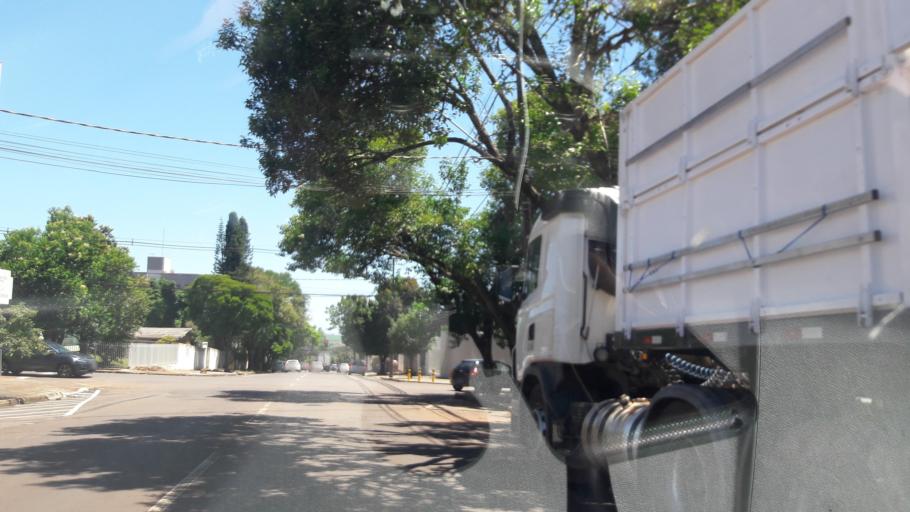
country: BR
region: Parana
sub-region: Cascavel
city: Cascavel
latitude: -24.9528
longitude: -53.4752
